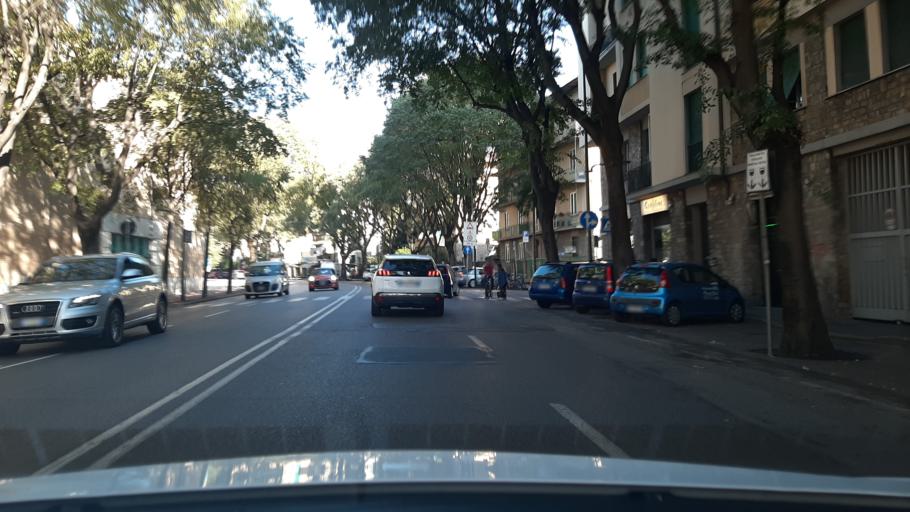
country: IT
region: Tuscany
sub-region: Province of Florence
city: Florence
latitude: 43.7904
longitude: 11.2296
